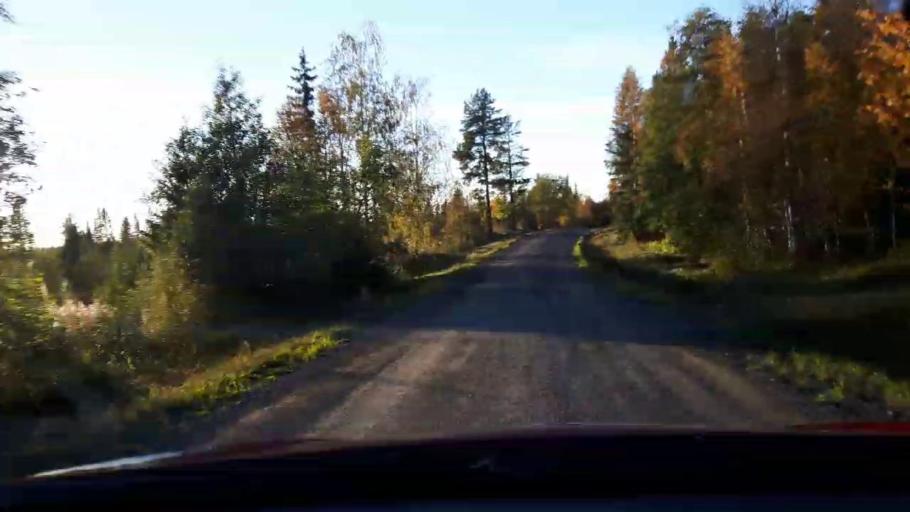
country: SE
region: Jaemtland
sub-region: Krokoms Kommun
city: Krokom
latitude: 63.4176
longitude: 14.6098
